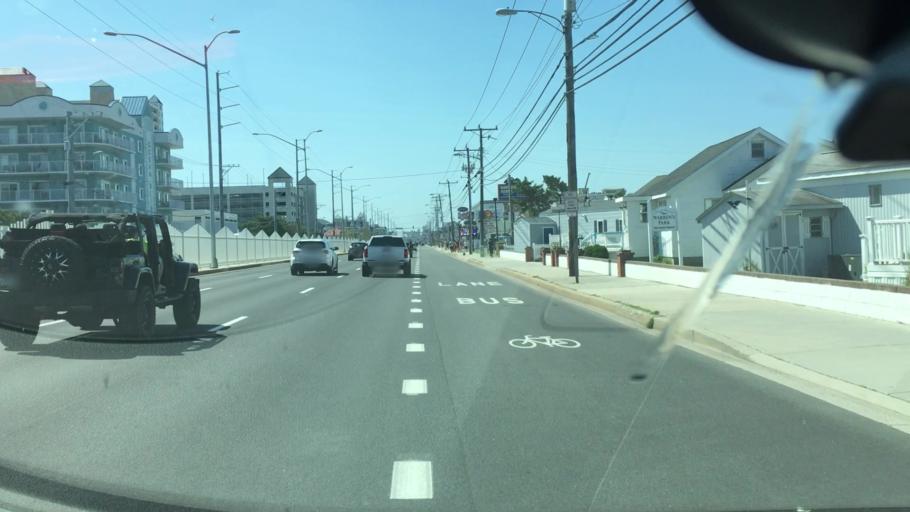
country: US
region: Maryland
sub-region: Worcester County
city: Ocean City
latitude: 38.3768
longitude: -75.0691
